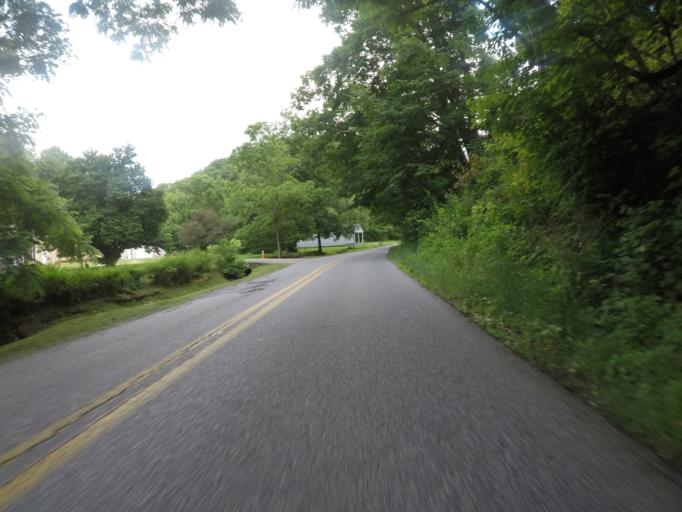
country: US
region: West Virginia
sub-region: Cabell County
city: Pea Ridge
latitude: 38.3987
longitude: -82.3621
